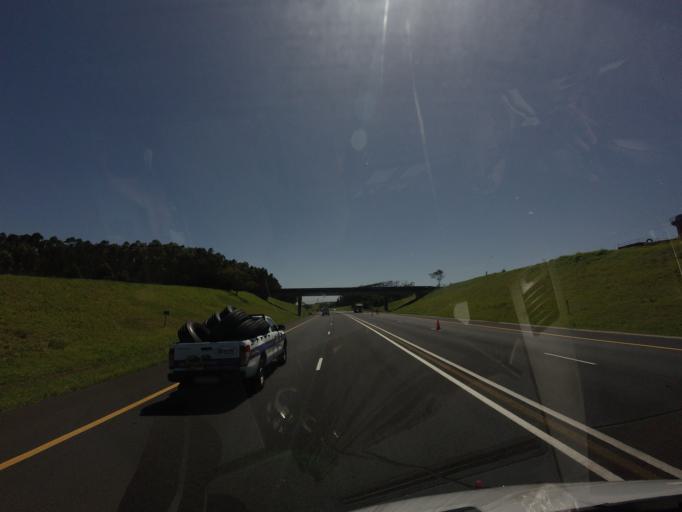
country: ZA
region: KwaZulu-Natal
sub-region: uThungulu District Municipality
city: eSikhawini
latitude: -28.9780
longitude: 31.7215
